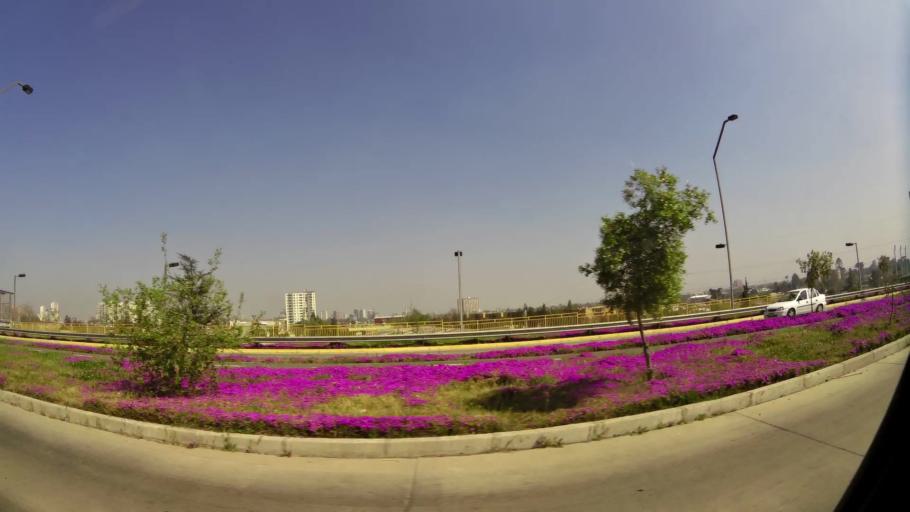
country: CL
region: Santiago Metropolitan
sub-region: Provincia de Santiago
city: Lo Prado
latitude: -33.4208
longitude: -70.6868
